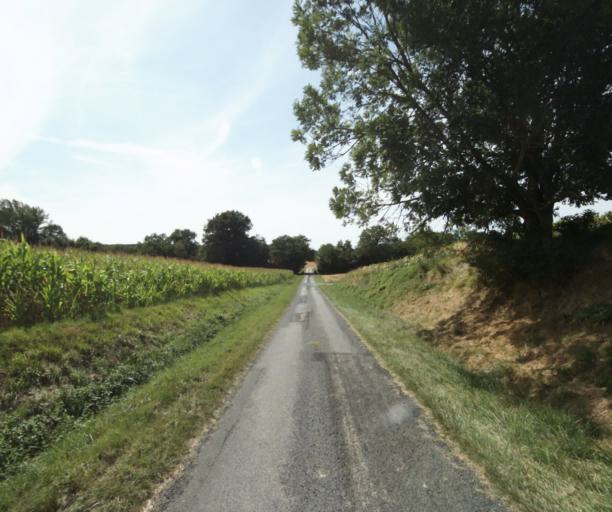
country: FR
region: Midi-Pyrenees
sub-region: Departement du Tarn
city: Soreze
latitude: 43.5118
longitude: 2.0716
